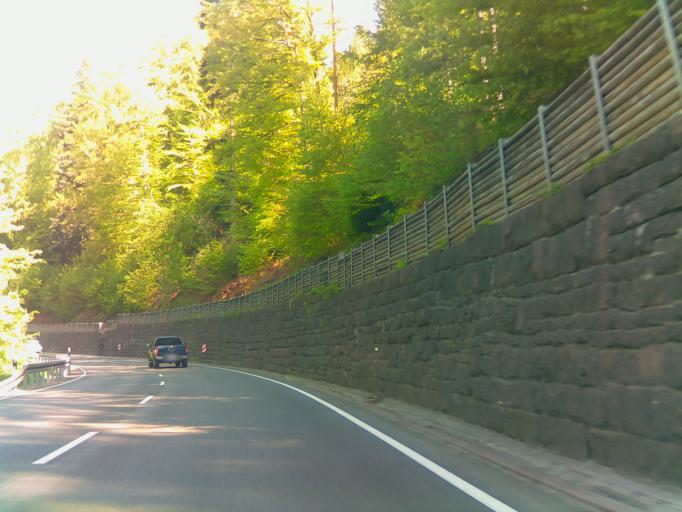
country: DE
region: Baden-Wuerttemberg
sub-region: Karlsruhe Region
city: Hofen an der Enz
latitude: 48.8114
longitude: 8.5836
